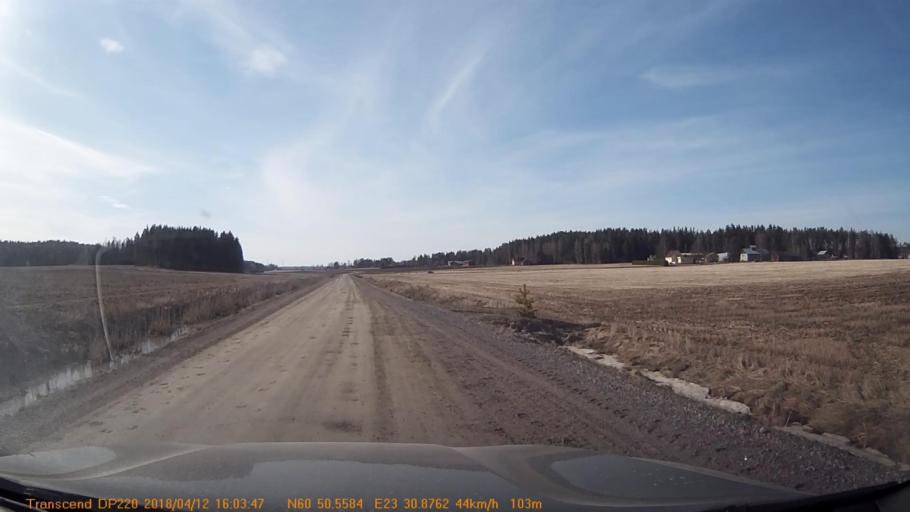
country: FI
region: Haeme
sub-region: Forssa
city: Jokioinen
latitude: 60.8427
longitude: 23.5144
